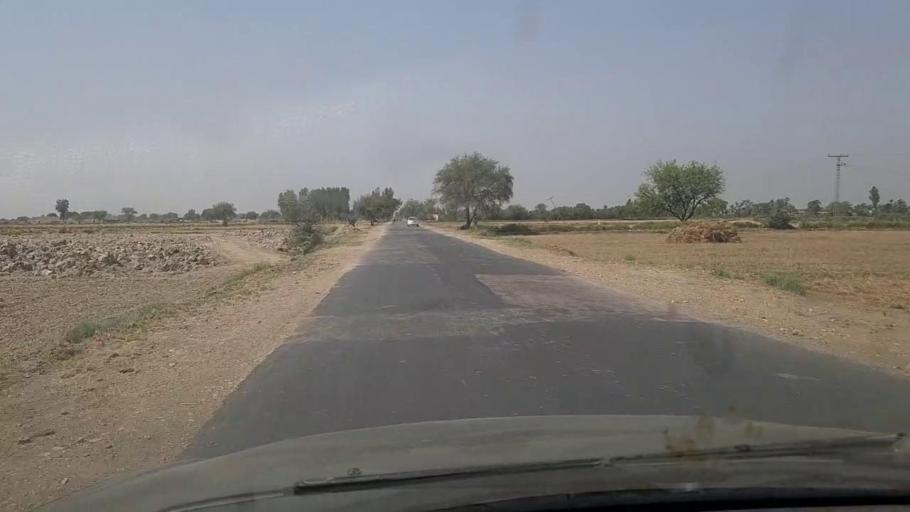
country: PK
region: Sindh
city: Khanpur
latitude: 27.8720
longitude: 69.4533
